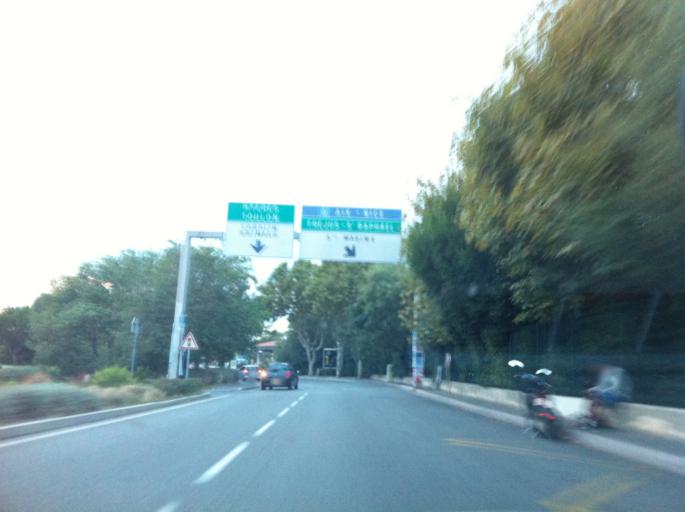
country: FR
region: Provence-Alpes-Cote d'Azur
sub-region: Departement du Var
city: Gassin
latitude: 43.2635
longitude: 6.5797
